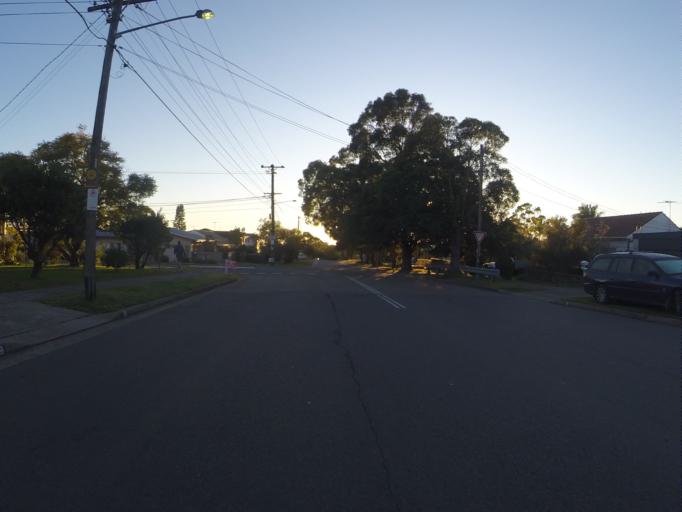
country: AU
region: New South Wales
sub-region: Sutherland Shire
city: Engadine
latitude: -34.0589
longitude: 151.0139
